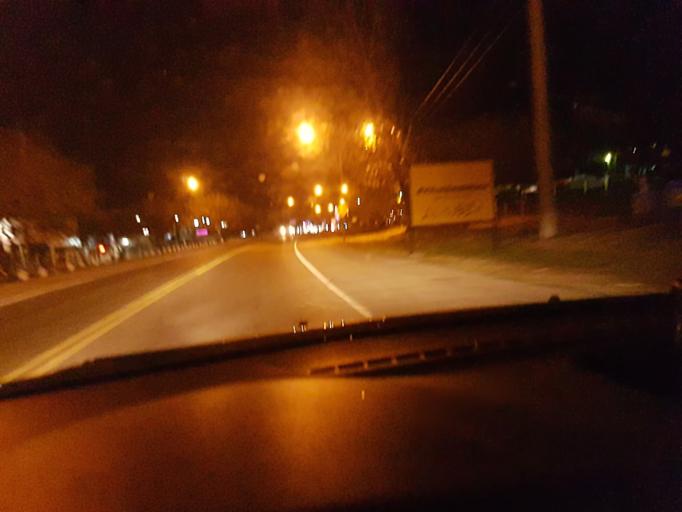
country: AR
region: Cordoba
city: Villa Allende
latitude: -31.3001
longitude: -64.2849
